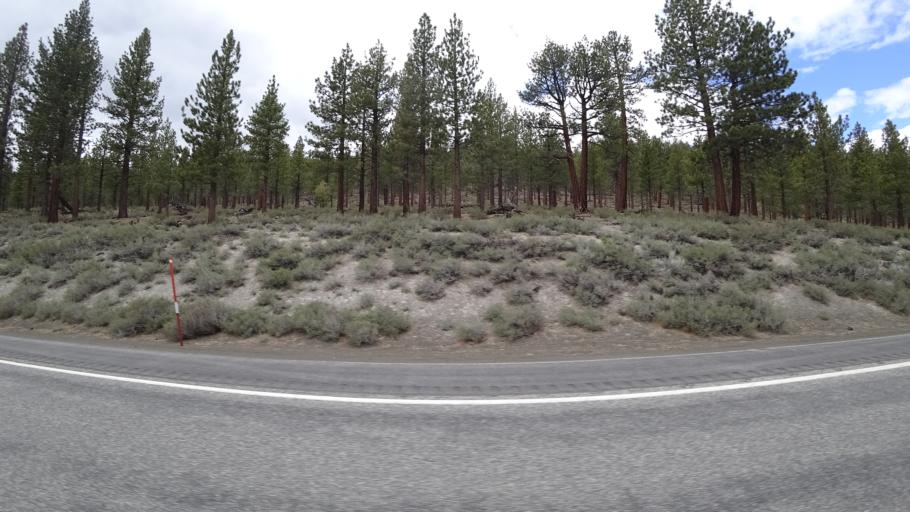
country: US
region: California
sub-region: Mono County
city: Mammoth Lakes
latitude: 37.7974
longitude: -119.0407
